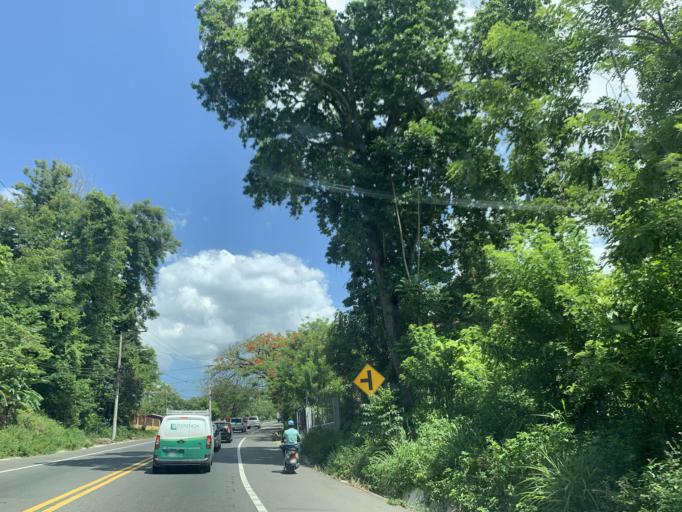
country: DO
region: Puerto Plata
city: Altamira
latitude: 19.6821
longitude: -70.8381
